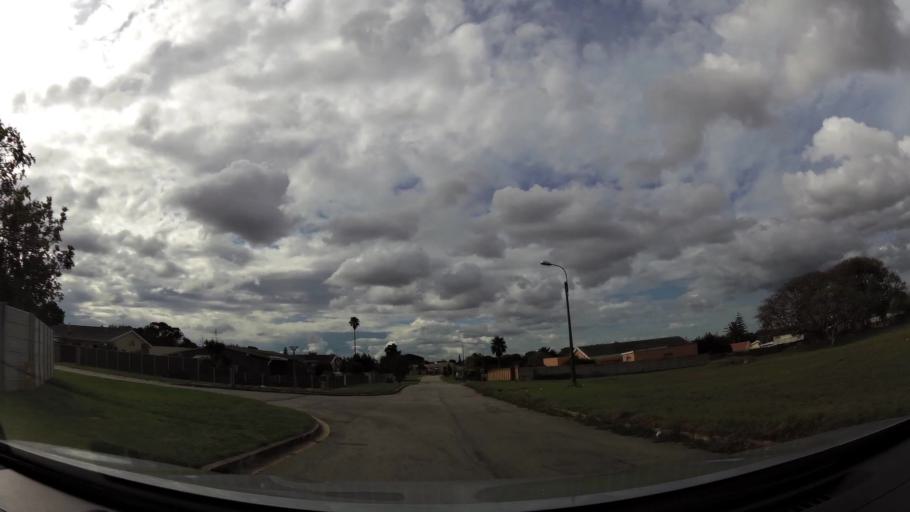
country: ZA
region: Eastern Cape
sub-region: Nelson Mandela Bay Metropolitan Municipality
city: Port Elizabeth
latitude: -33.9372
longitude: 25.5097
